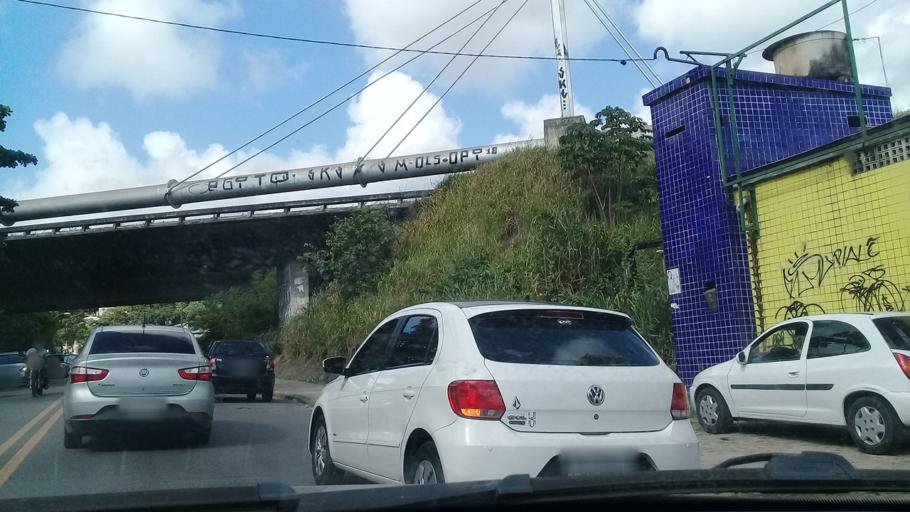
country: BR
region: Pernambuco
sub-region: Jaboatao Dos Guararapes
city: Jaboatao dos Guararapes
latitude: -8.1188
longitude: -34.9427
